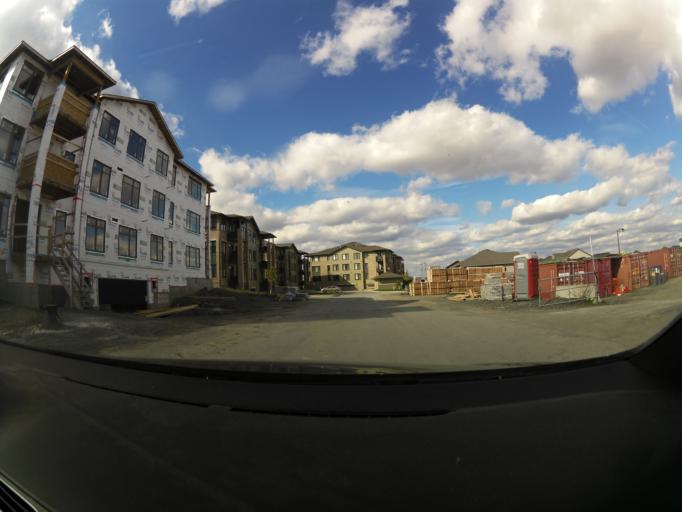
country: CA
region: Ontario
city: Bells Corners
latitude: 45.2691
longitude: -75.8897
